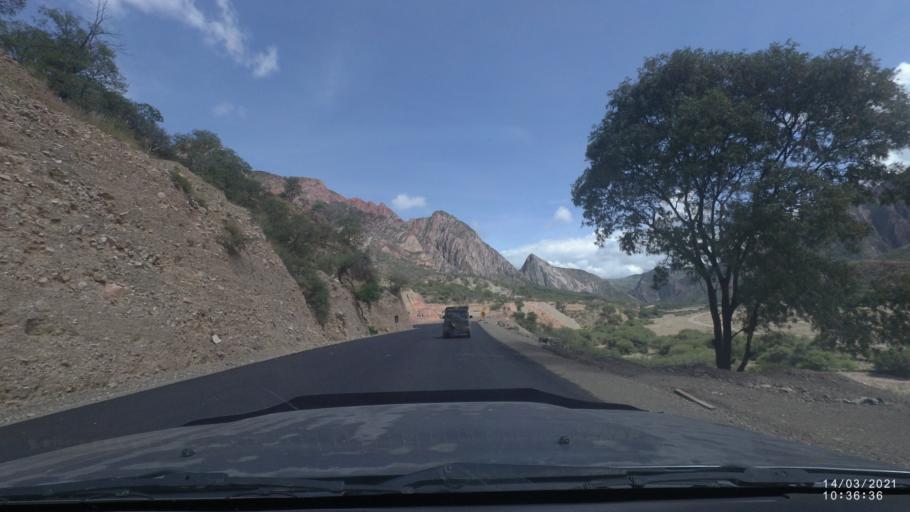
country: BO
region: Cochabamba
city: Cliza
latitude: -17.9014
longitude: -65.8851
